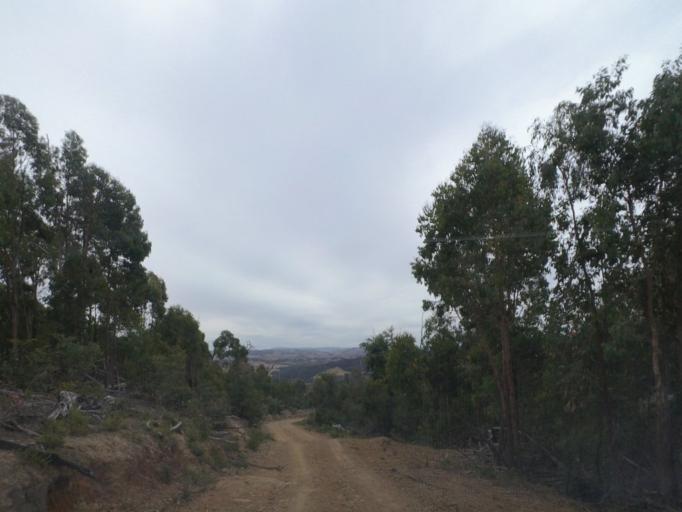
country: AU
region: Victoria
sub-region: Murrindindi
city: Alexandra
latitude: -37.3790
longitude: 145.5648
